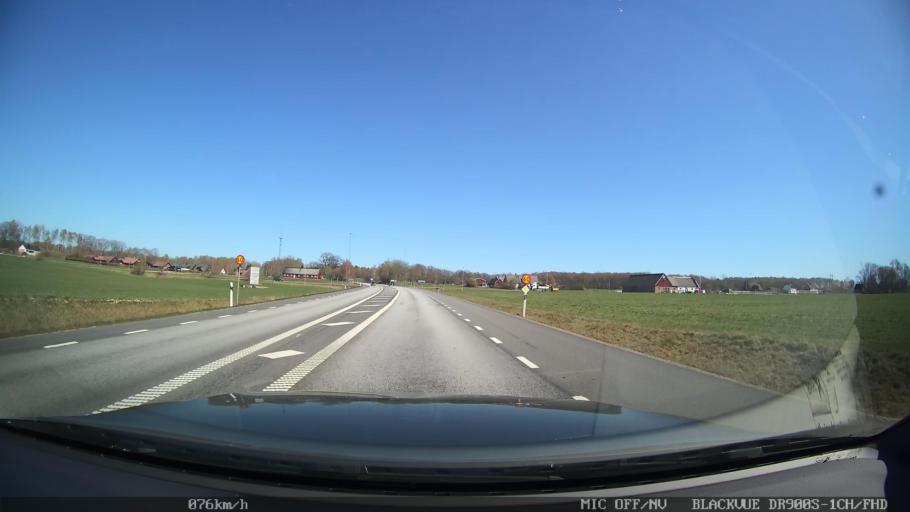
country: SE
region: Skane
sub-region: Klippans Kommun
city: Klippan
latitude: 56.1157
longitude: 13.1488
